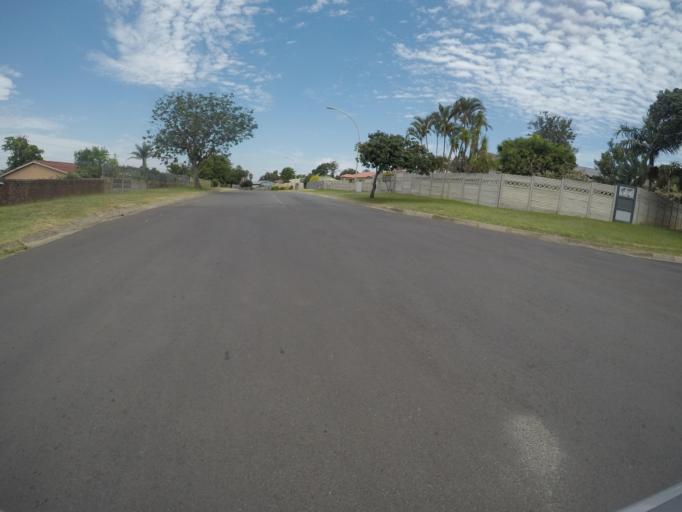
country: ZA
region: Eastern Cape
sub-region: Buffalo City Metropolitan Municipality
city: East London
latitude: -32.9803
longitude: 27.8671
